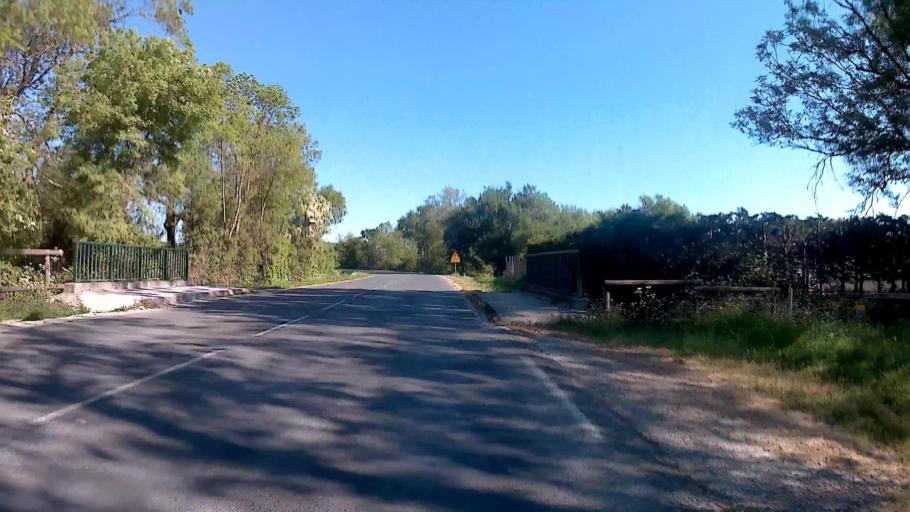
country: FR
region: Aquitaine
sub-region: Departement de la Gironde
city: Cadaujac
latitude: 44.7593
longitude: -0.5287
